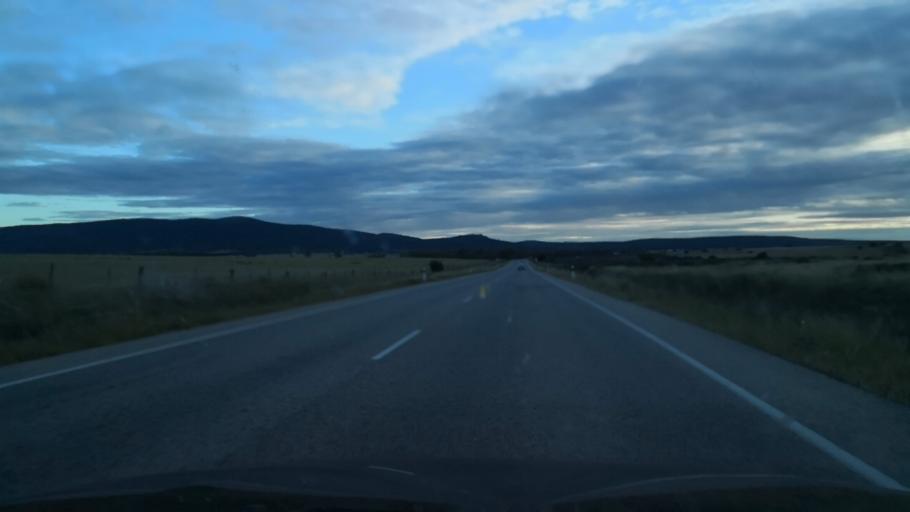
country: ES
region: Extremadura
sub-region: Provincia de Caceres
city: Malpartida de Caceres
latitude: 39.3397
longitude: -6.4785
